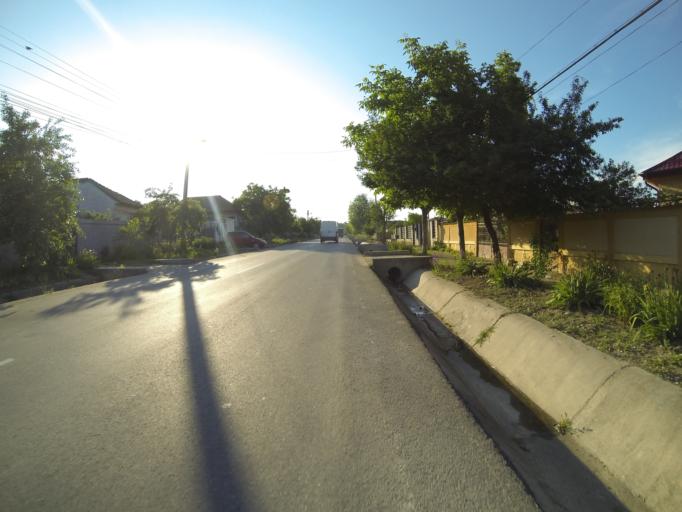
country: RO
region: Dolj
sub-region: Comuna Podari
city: Podari
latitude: 44.2421
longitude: 23.7820
